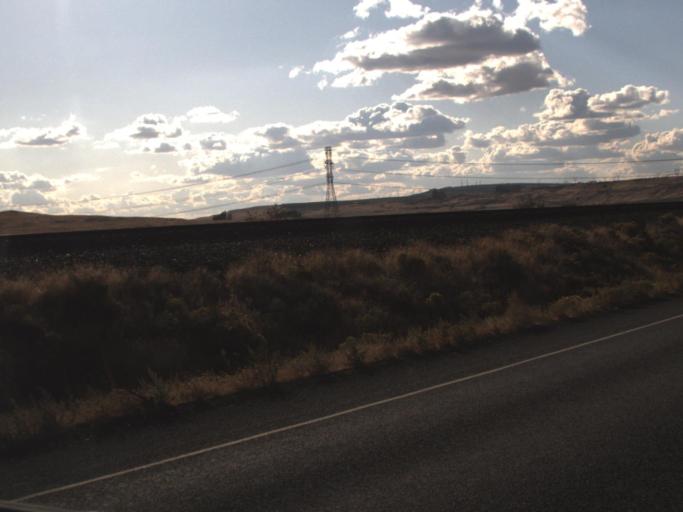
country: US
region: Oregon
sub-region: Morrow County
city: Boardman
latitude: 45.8681
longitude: -119.8158
